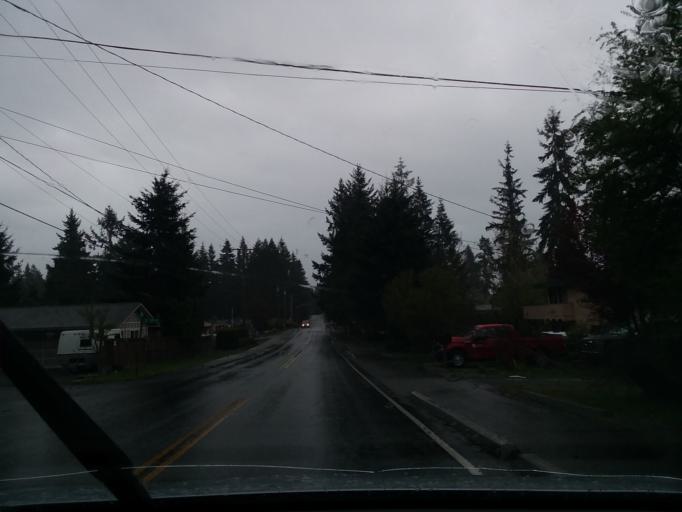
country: US
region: Washington
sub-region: King County
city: Fairwood
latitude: 47.4781
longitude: -122.1483
